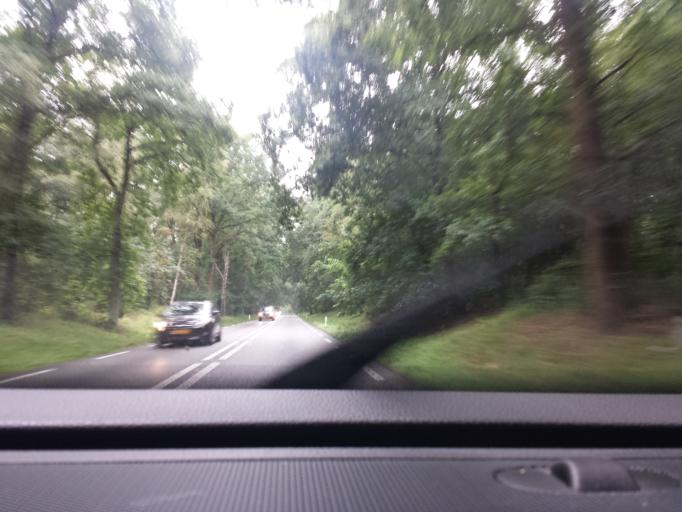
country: NL
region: Gelderland
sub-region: Gemeente Montferland
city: s-Heerenberg
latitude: 51.8927
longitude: 6.2563
